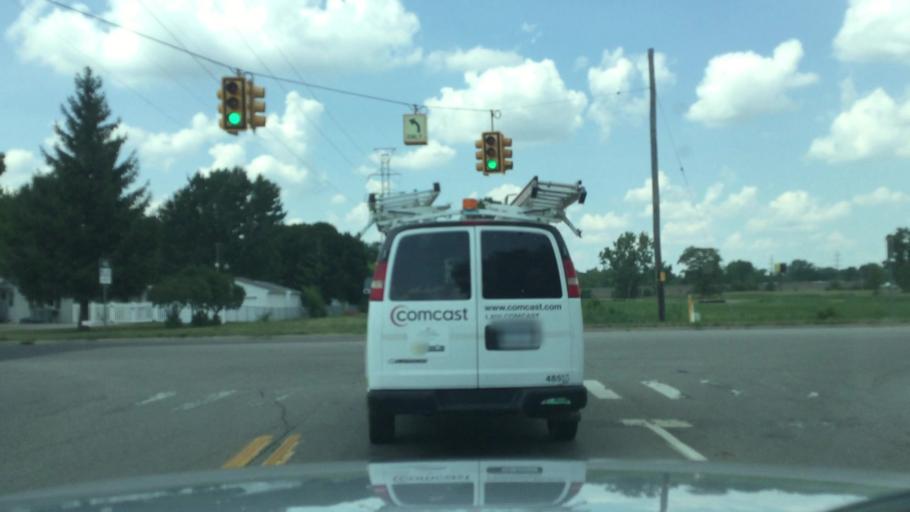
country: US
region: Michigan
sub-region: Washtenaw County
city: Ypsilanti
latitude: 42.2135
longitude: -83.5580
